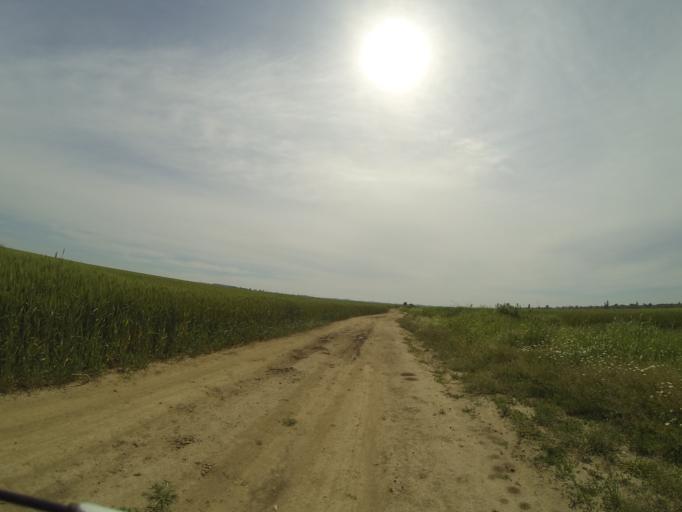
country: RO
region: Dolj
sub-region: Comuna Malu Mare
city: Preajba
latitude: 44.2721
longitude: 23.8489
